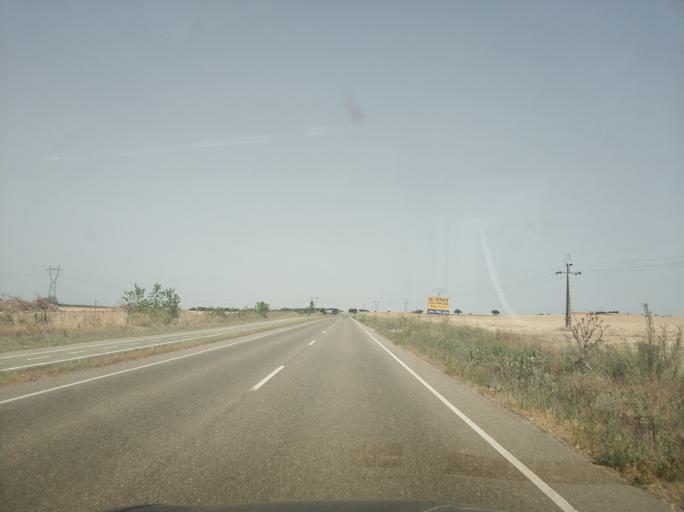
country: ES
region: Castille and Leon
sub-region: Provincia de Salamanca
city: Villamayor
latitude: 41.0252
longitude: -5.7240
